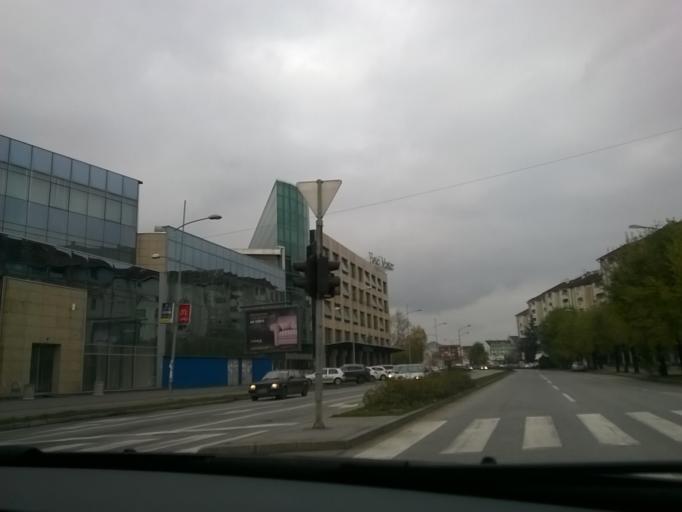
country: RS
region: Autonomna Pokrajina Vojvodina
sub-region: Juznobacki Okrug
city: Novi Sad
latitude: 45.2590
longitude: 19.8226
